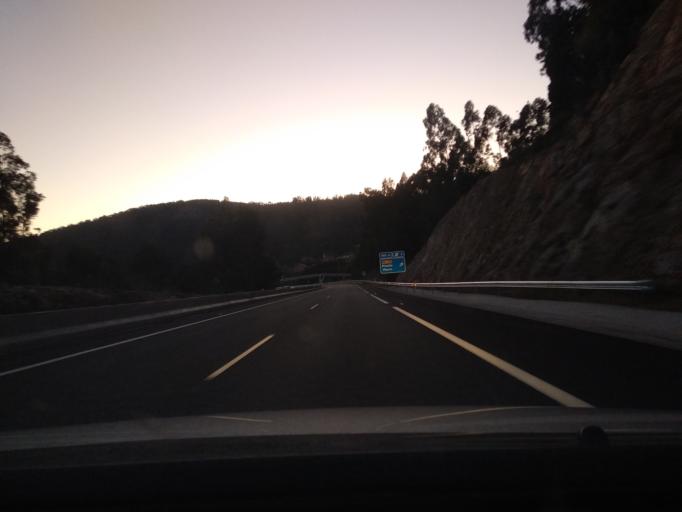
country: ES
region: Galicia
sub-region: Provincia de Pontevedra
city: Moana
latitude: 42.3085
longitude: -8.7345
